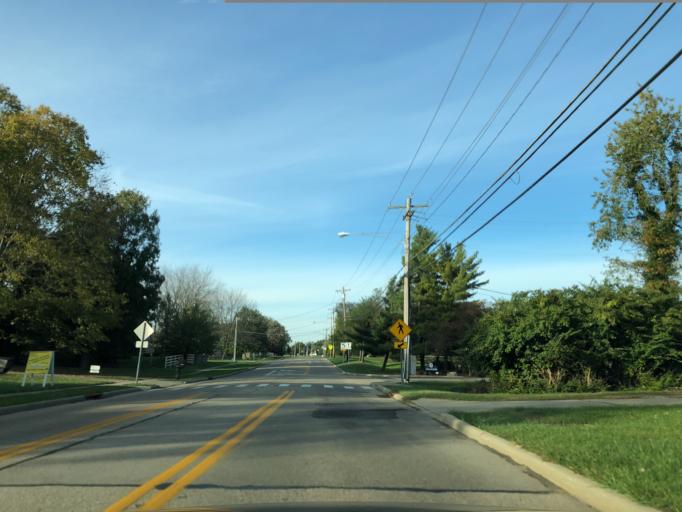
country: US
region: Ohio
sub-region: Hamilton County
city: Loveland
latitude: 39.2752
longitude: -84.2733
